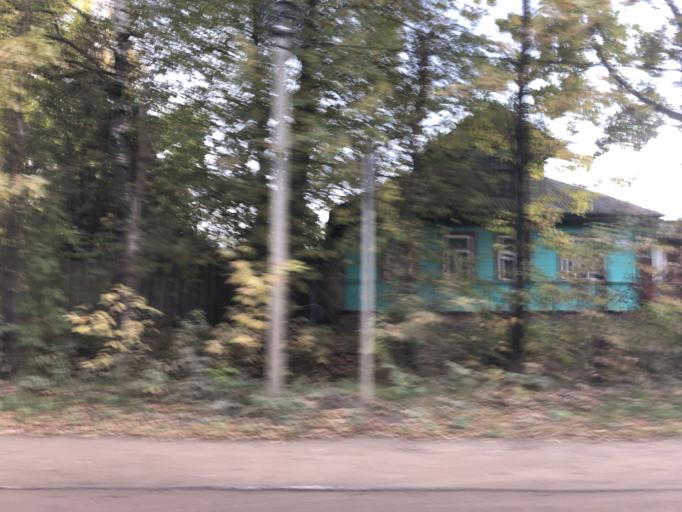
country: RU
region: Tverskaya
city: Rzhev
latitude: 56.2491
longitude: 34.3009
